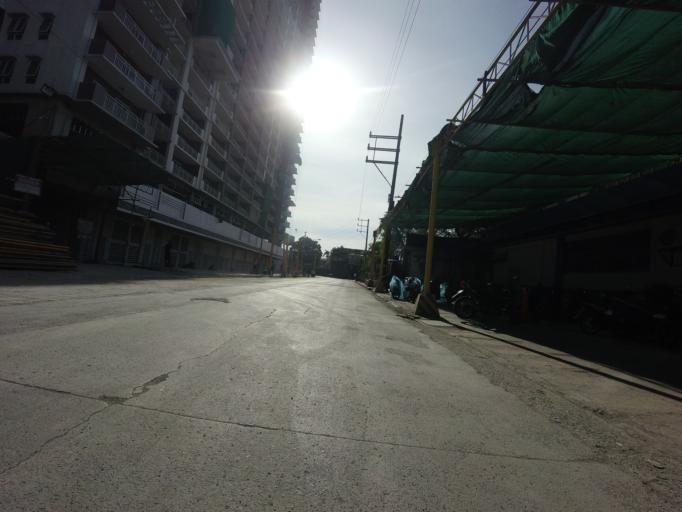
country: PH
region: Metro Manila
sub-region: Pasig
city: Pasig City
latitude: 14.5691
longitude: 121.0546
